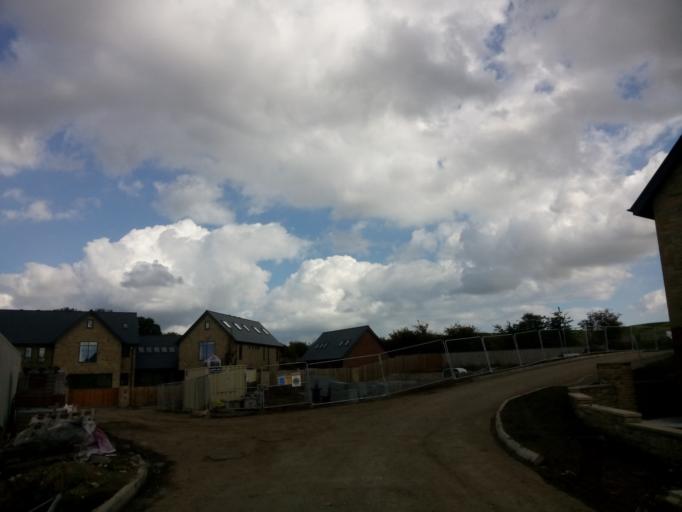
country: GB
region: England
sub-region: County Durham
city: West Rainton
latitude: 54.7912
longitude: -1.5169
